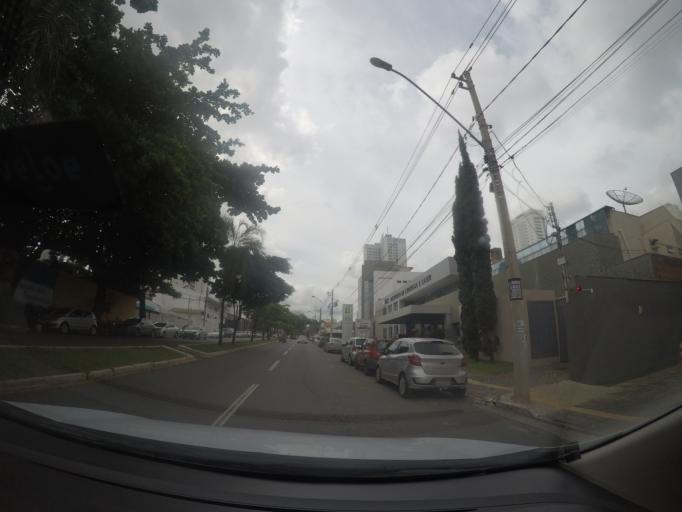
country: BR
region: Goias
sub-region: Goiania
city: Goiania
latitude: -16.7028
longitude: -49.2724
